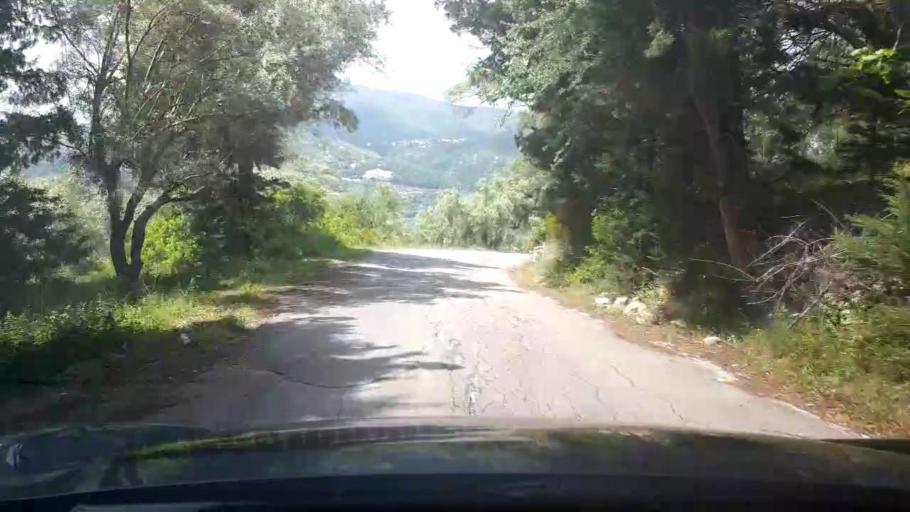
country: GR
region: Ionian Islands
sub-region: Lefkada
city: Nidri
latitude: 38.6448
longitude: 20.7054
